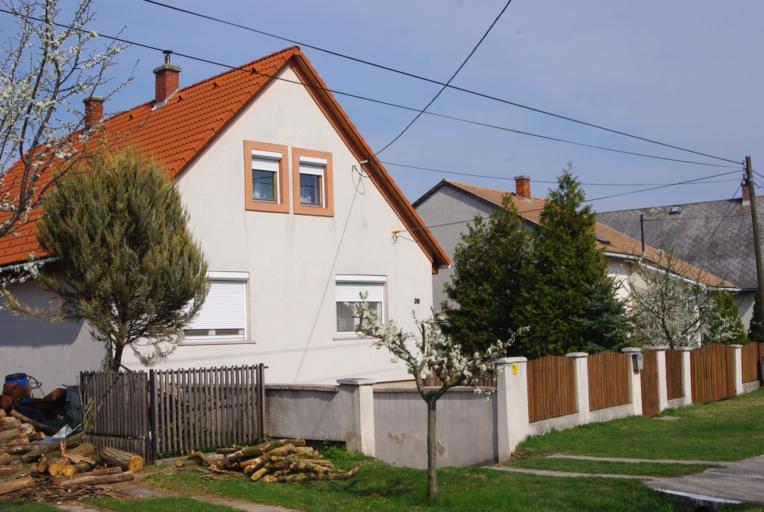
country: HU
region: Fejer
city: Csakvar
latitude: 47.4338
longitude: 18.5176
